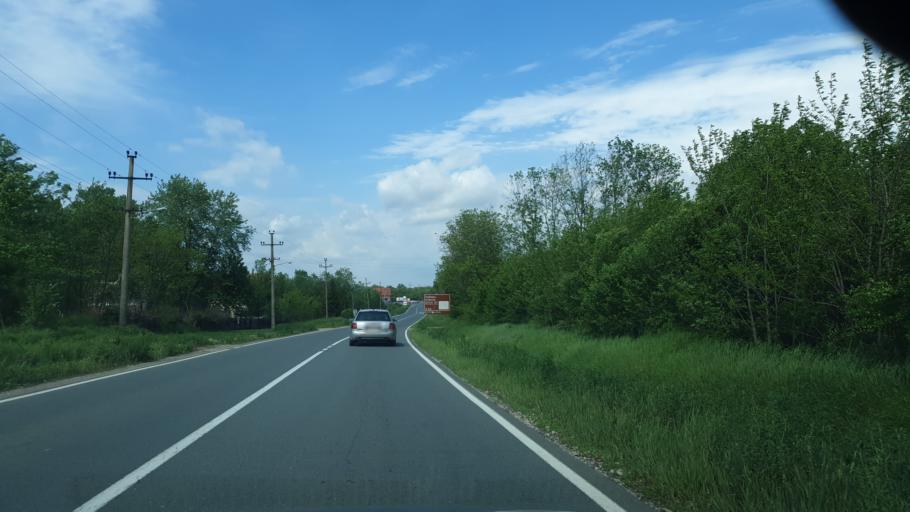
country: RS
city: Stubline
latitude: 44.6044
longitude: 20.1504
